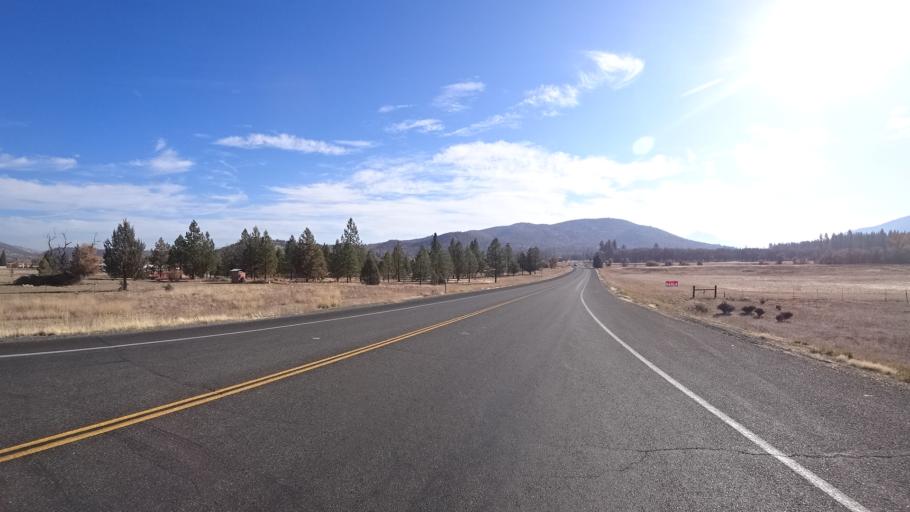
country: US
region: California
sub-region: Siskiyou County
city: Yreka
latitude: 41.6965
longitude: -122.6482
